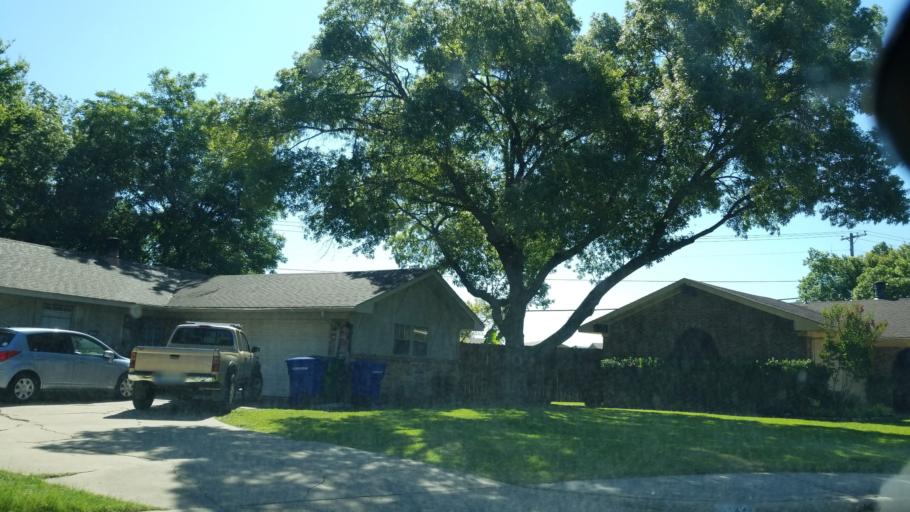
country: US
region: Texas
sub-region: Dallas County
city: Carrollton
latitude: 32.9590
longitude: -96.8893
